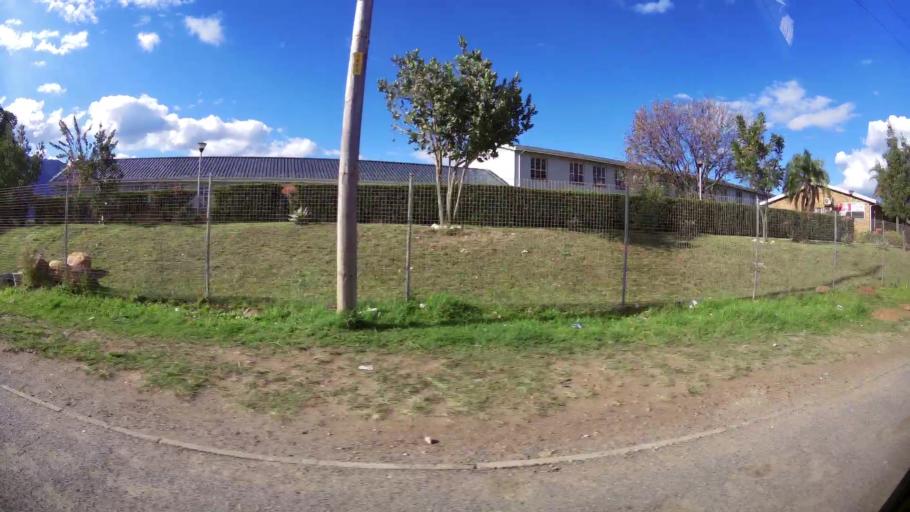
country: ZA
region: Western Cape
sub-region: Overberg District Municipality
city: Swellendam
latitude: -34.0410
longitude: 20.4443
